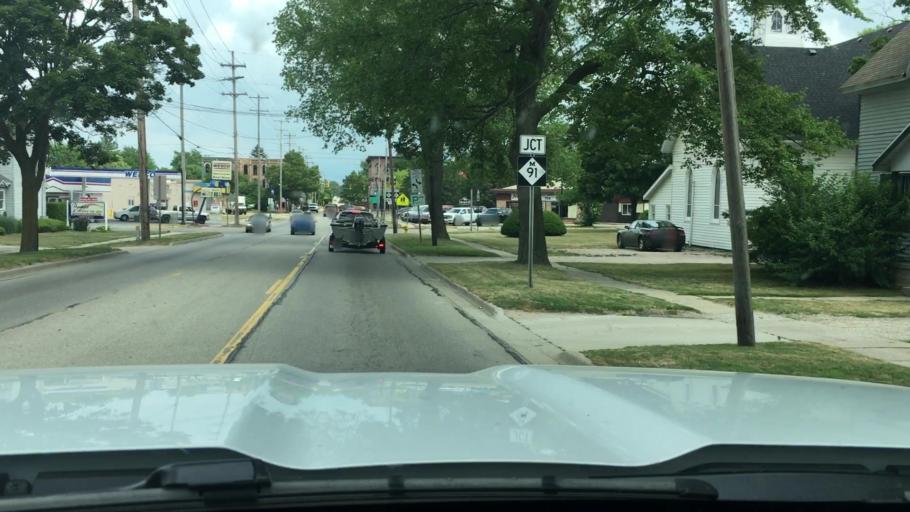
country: US
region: Michigan
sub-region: Montcalm County
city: Greenville
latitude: 43.1774
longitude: -85.2557
